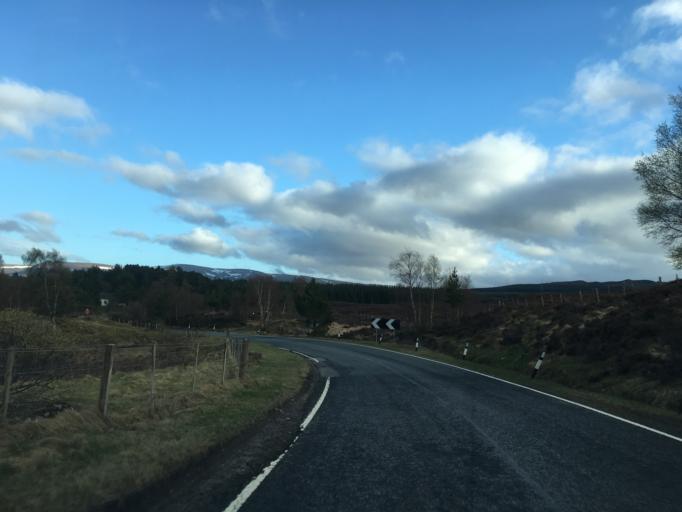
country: GB
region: Scotland
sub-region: Highland
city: Kingussie
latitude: 56.9915
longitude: -4.2495
